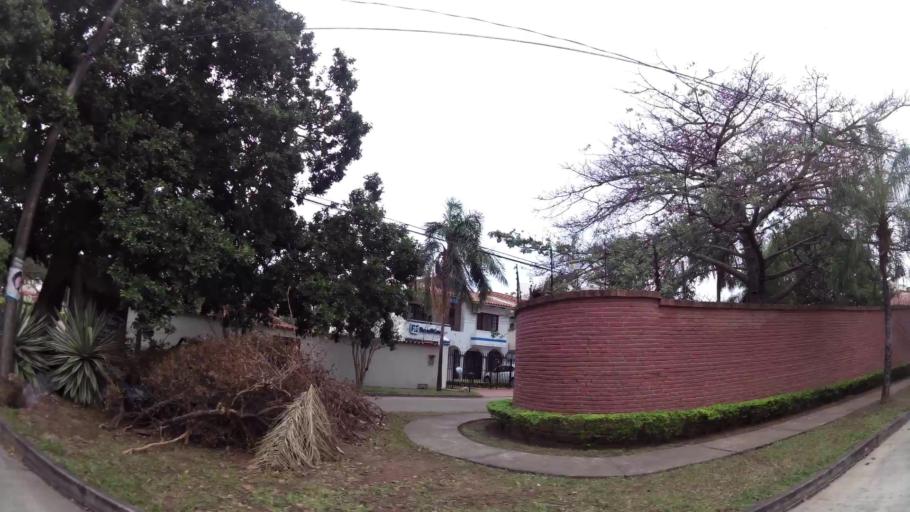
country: BO
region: Santa Cruz
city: Santa Cruz de la Sierra
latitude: -17.7660
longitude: -63.1745
